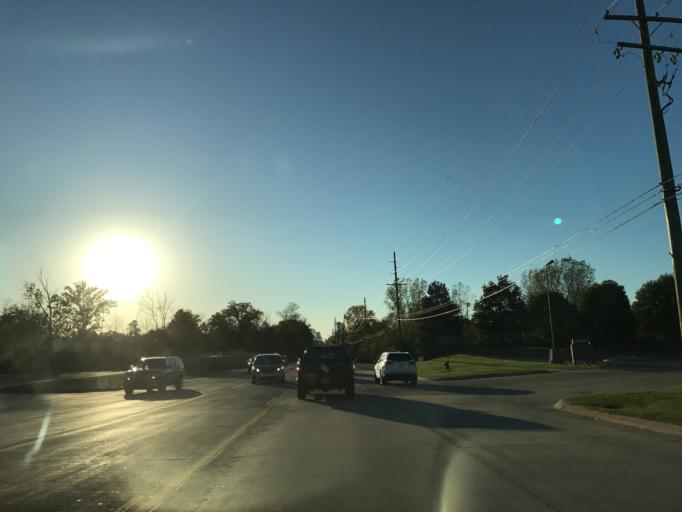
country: US
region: Michigan
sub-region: Oakland County
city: Novi
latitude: 42.4666
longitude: -83.4766
